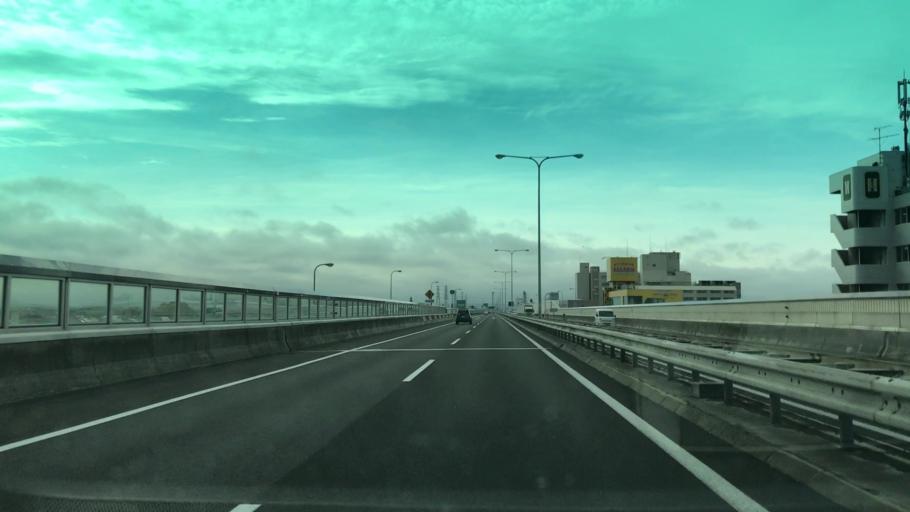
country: JP
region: Hokkaido
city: Sapporo
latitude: 43.0981
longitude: 141.3919
